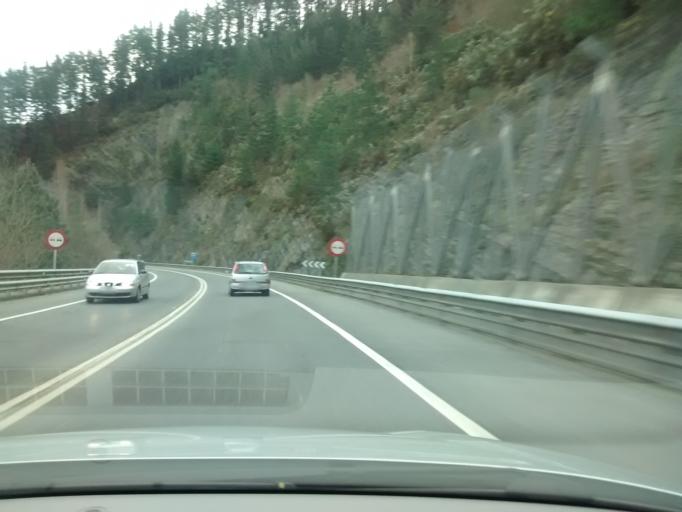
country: ES
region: Basque Country
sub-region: Bizkaia
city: Urrestieta
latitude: 43.1975
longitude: -3.1563
